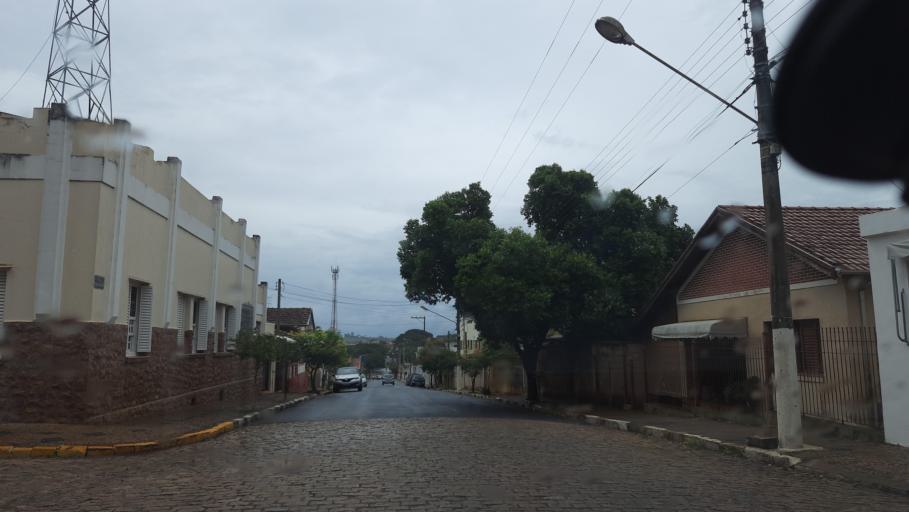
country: BR
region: Sao Paulo
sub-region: Casa Branca
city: Casa Branca
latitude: -21.7701
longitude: -47.0889
